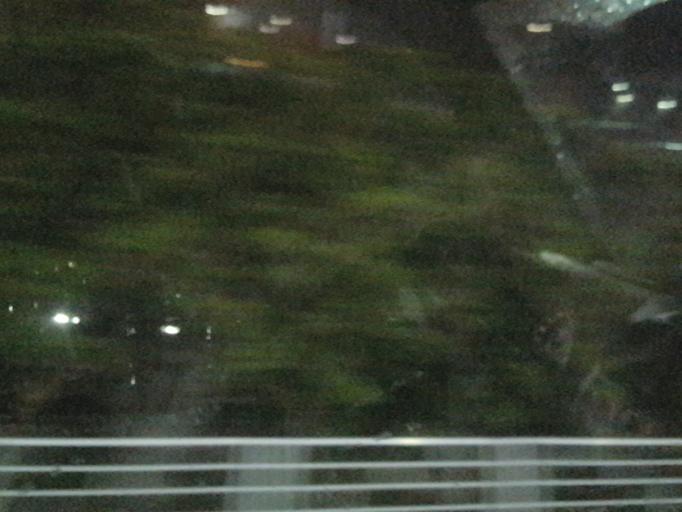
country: IN
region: Telangana
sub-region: Rangareddi
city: Kukatpalli
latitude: 17.4444
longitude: 78.3773
